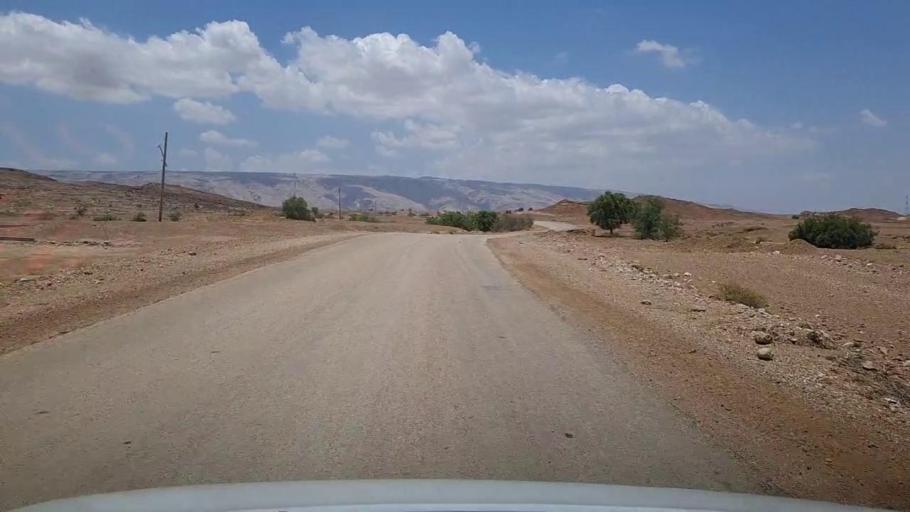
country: PK
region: Sindh
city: Bhan
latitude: 26.3178
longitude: 67.5610
